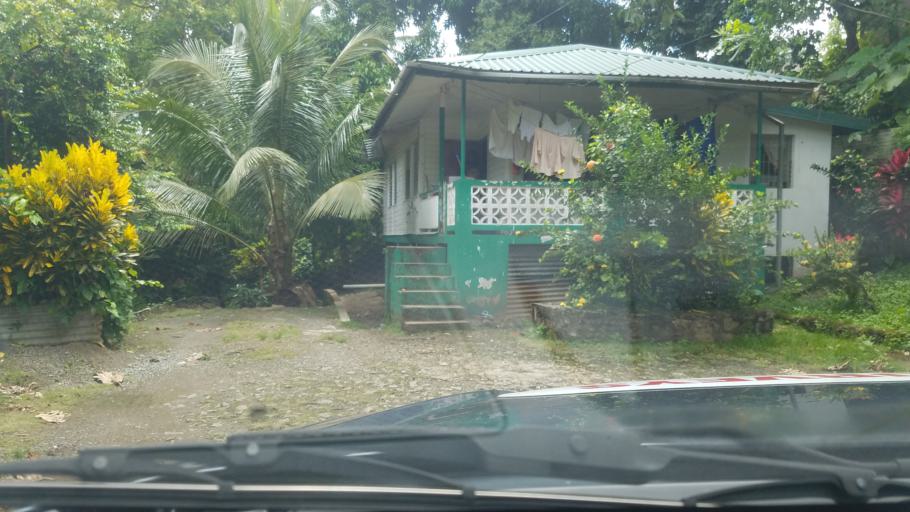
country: LC
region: Castries Quarter
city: Bisee
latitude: 14.0030
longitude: -60.9760
